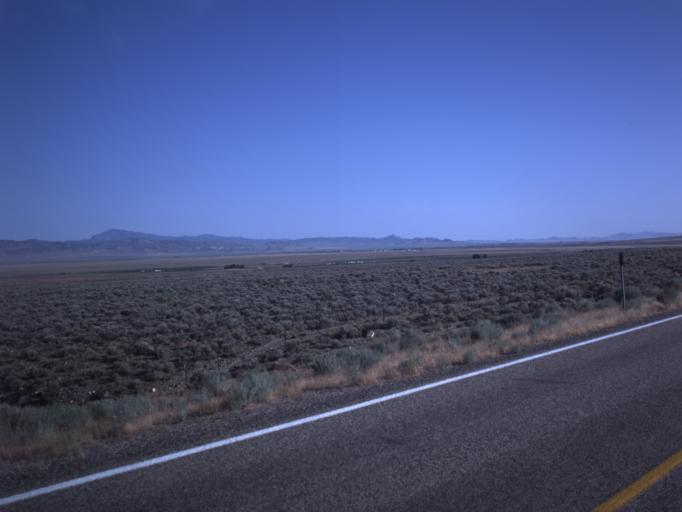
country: US
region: Utah
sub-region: Beaver County
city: Milford
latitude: 38.1655
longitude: -112.9546
